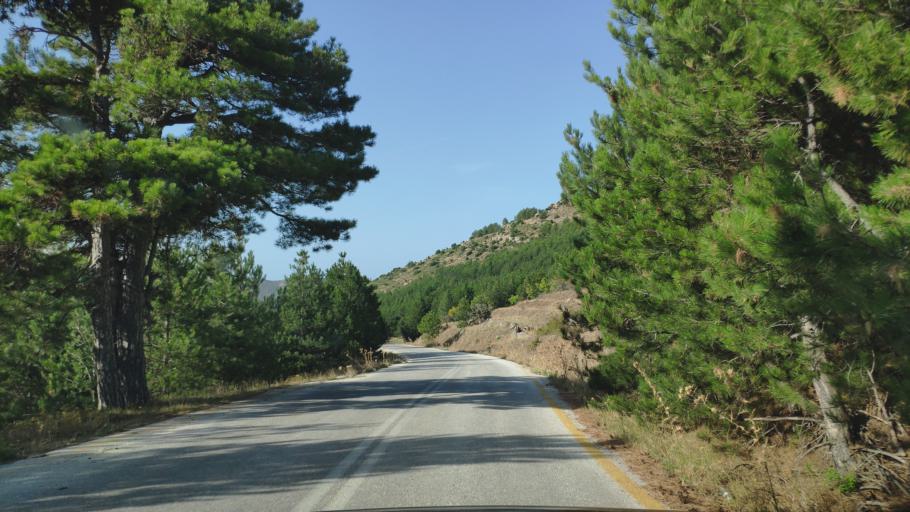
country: GR
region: West Greece
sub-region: Nomos Achaias
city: Aiyira
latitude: 38.0476
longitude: 22.3861
